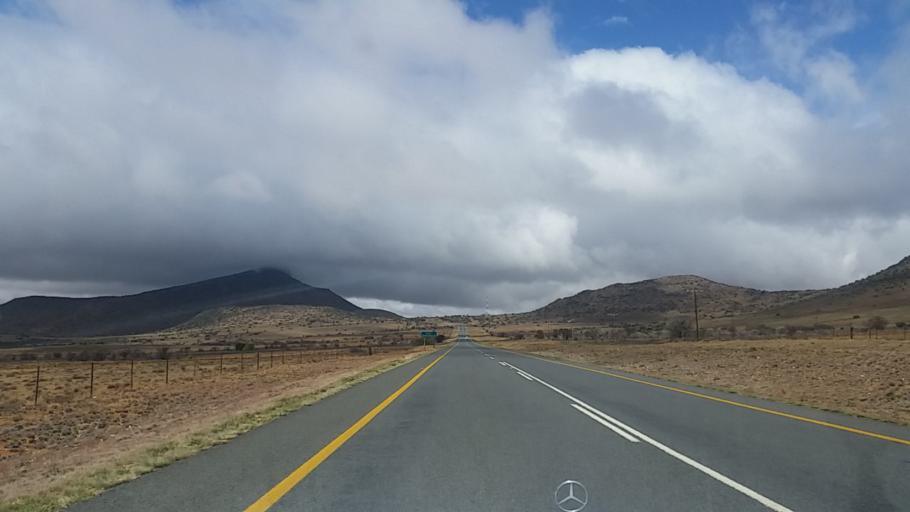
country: ZA
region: Eastern Cape
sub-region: Cacadu District Municipality
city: Graaff-Reinet
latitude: -32.0935
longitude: 24.6040
